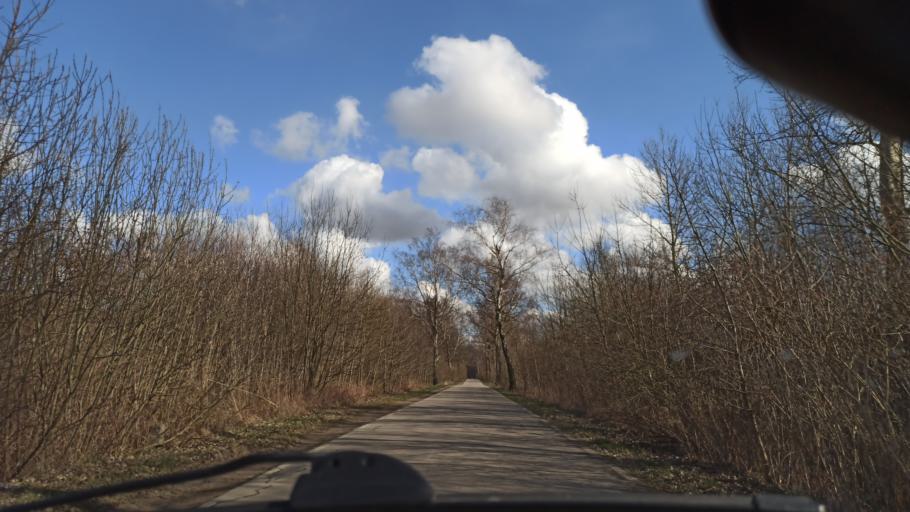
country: PL
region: Warmian-Masurian Voivodeship
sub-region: Powiat elblaski
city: Tolkmicko
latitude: 54.2633
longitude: 19.4893
